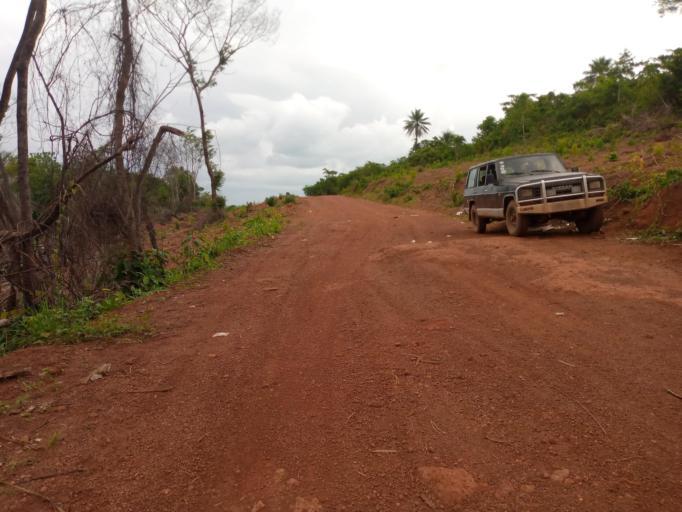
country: SL
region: Southern Province
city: Moyamba
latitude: 8.0758
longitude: -12.4542
